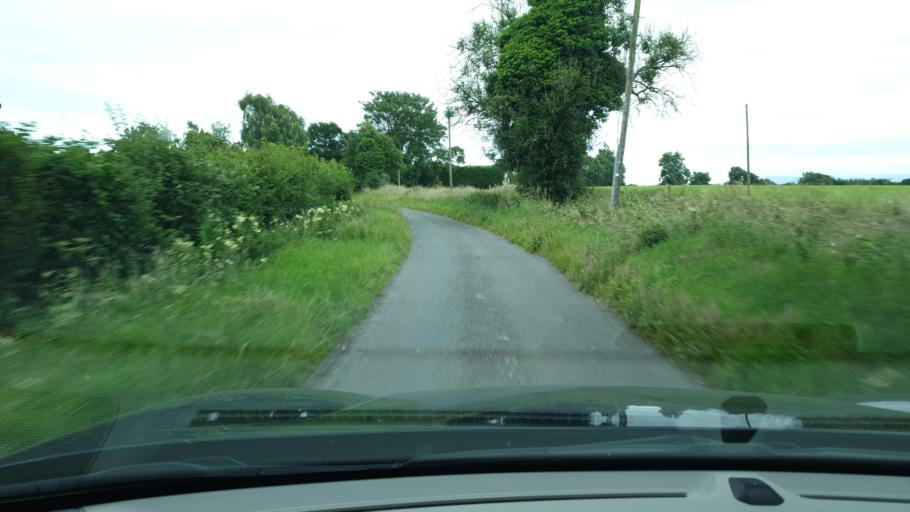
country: IE
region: Leinster
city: Ballymun
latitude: 53.4318
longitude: -6.2894
